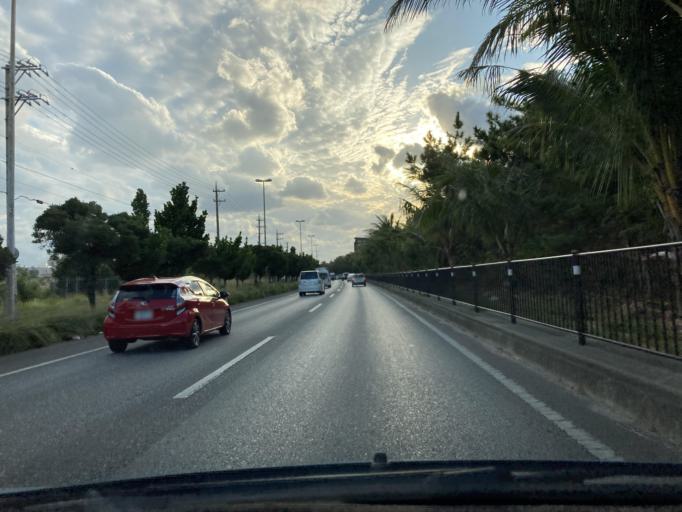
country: JP
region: Okinawa
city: Ginowan
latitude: 26.2849
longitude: 127.7468
